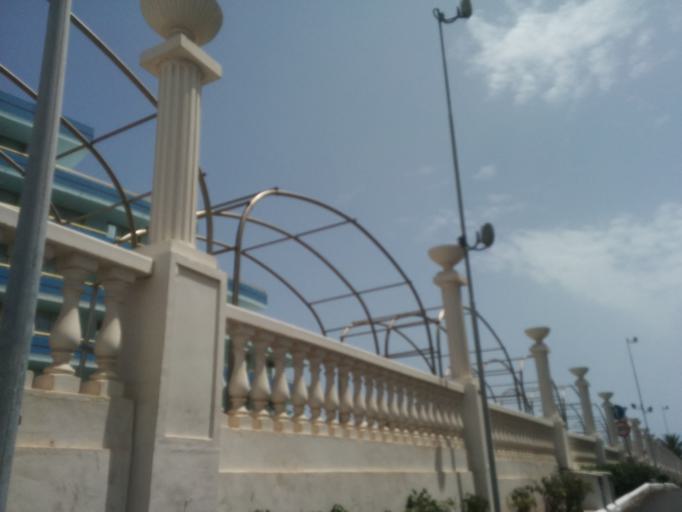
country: ES
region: Canary Islands
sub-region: Provincia de Santa Cruz de Tenerife
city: Playa de las Americas
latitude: 28.0544
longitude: -16.7306
